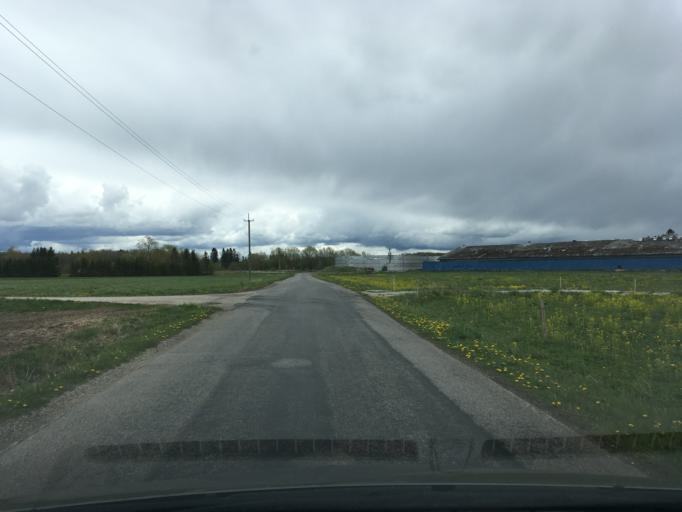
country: EE
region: Harju
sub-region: Joelaehtme vald
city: Loo
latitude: 59.3665
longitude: 24.9666
